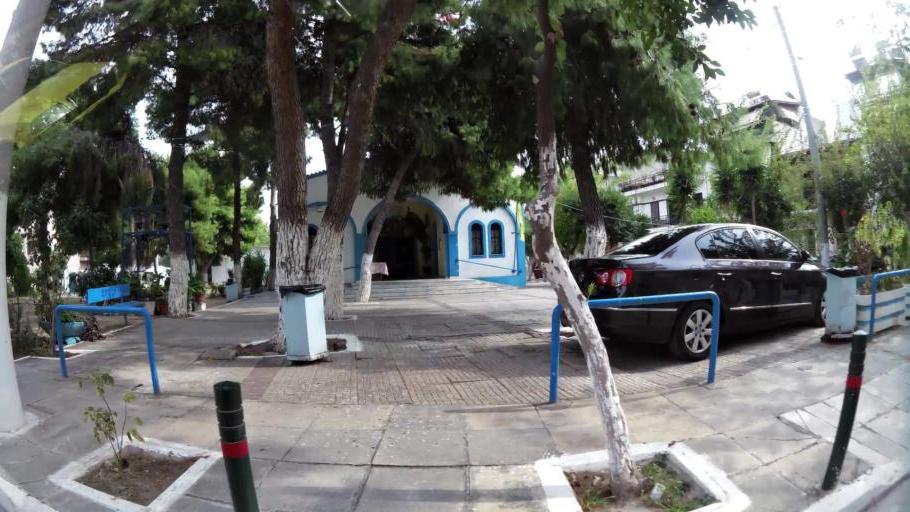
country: GR
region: Attica
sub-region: Nomarchia Athinas
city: Peristeri
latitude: 38.0115
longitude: 23.6810
